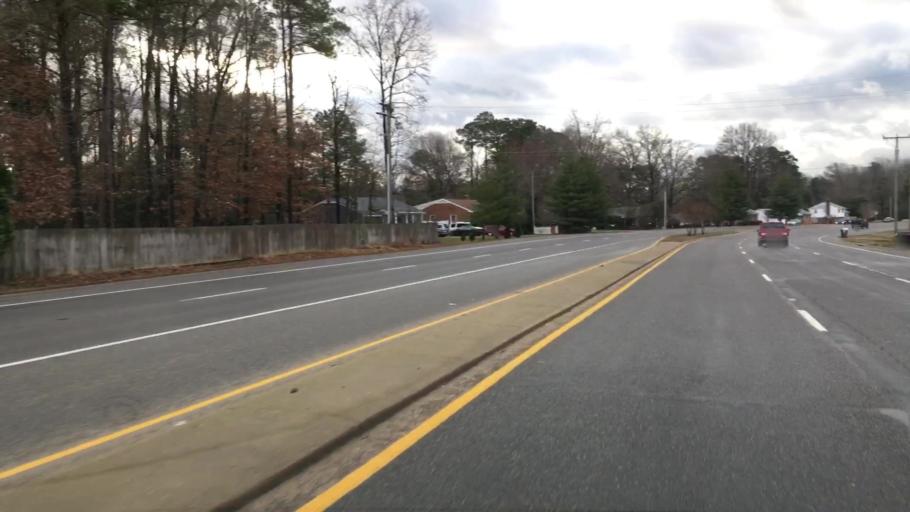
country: US
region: Virginia
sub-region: Chesterfield County
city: Bon Air
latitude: 37.4798
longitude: -77.5971
